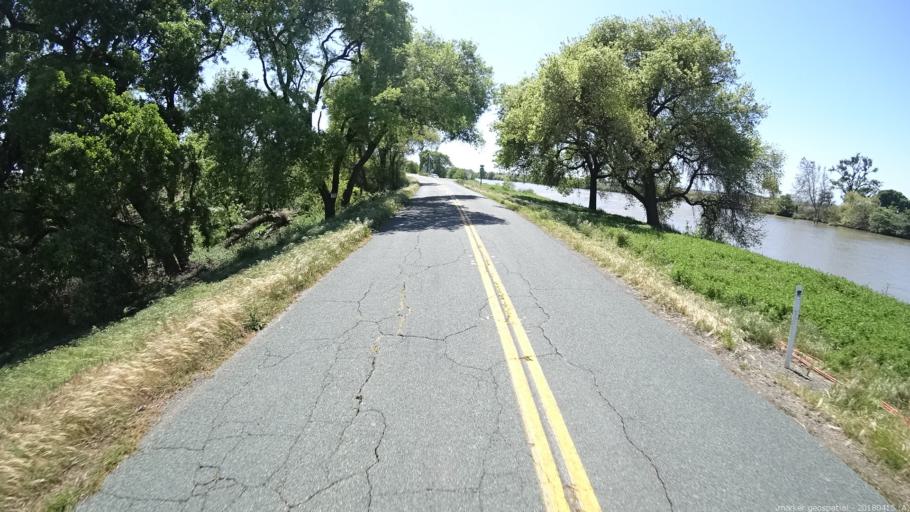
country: US
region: California
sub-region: Sacramento County
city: Walnut Grove
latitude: 38.2378
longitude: -121.6022
